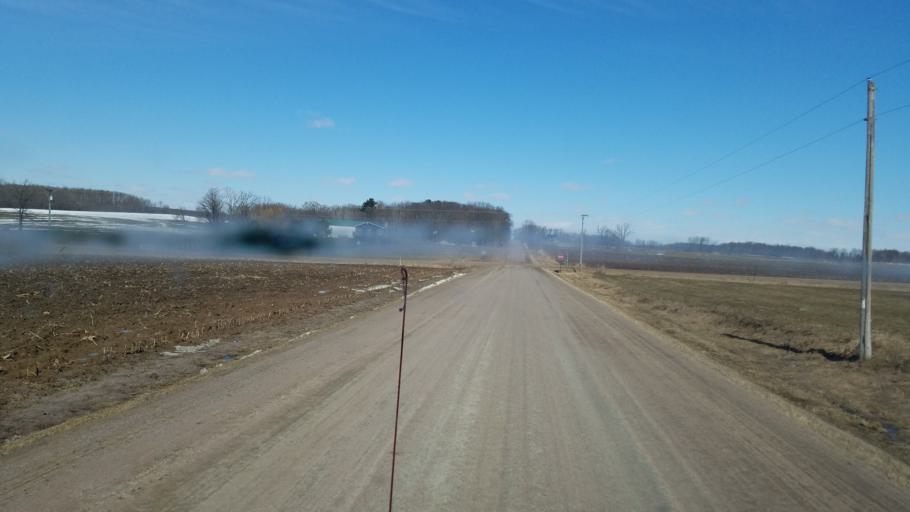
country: US
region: Wisconsin
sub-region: Clark County
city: Loyal
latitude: 44.6250
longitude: -90.3971
